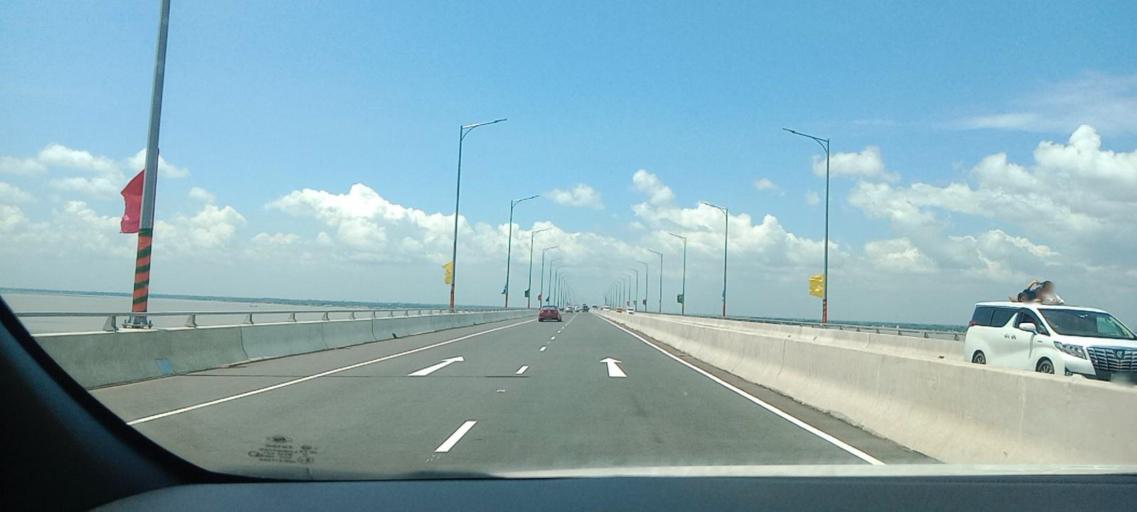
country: BD
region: Dhaka
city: Char Bhadrasan
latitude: 23.4408
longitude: 90.2611
